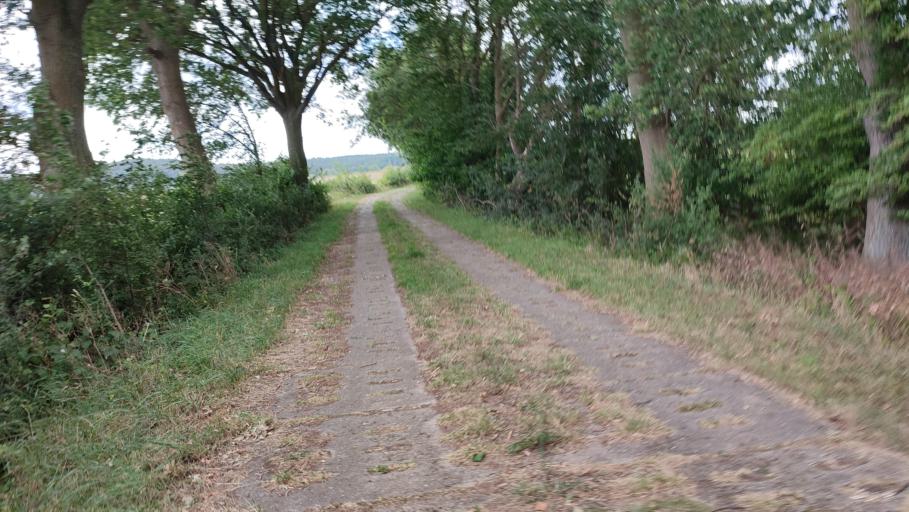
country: DE
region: Lower Saxony
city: Neu Darchau
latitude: 53.2099
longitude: 10.9697
